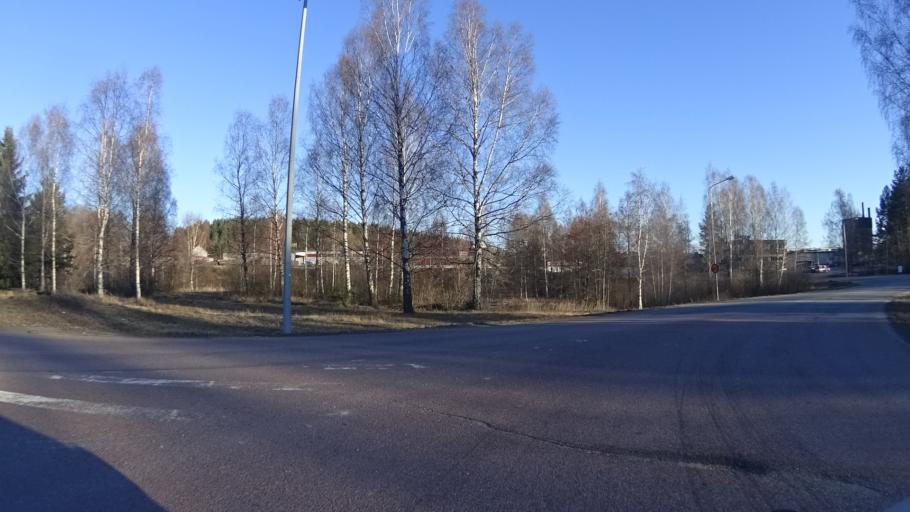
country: SE
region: Vaermland
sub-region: Arvika Kommun
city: Arvika
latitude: 59.6619
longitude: 12.6259
